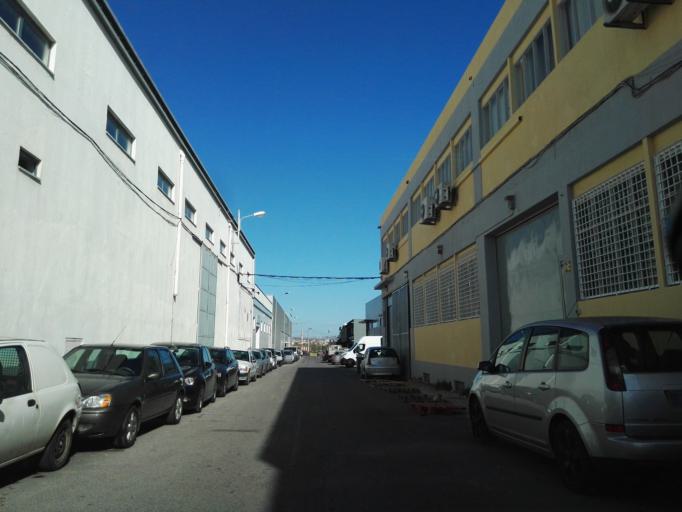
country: PT
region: Lisbon
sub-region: Loures
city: Camarate
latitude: 38.7855
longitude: -9.1310
